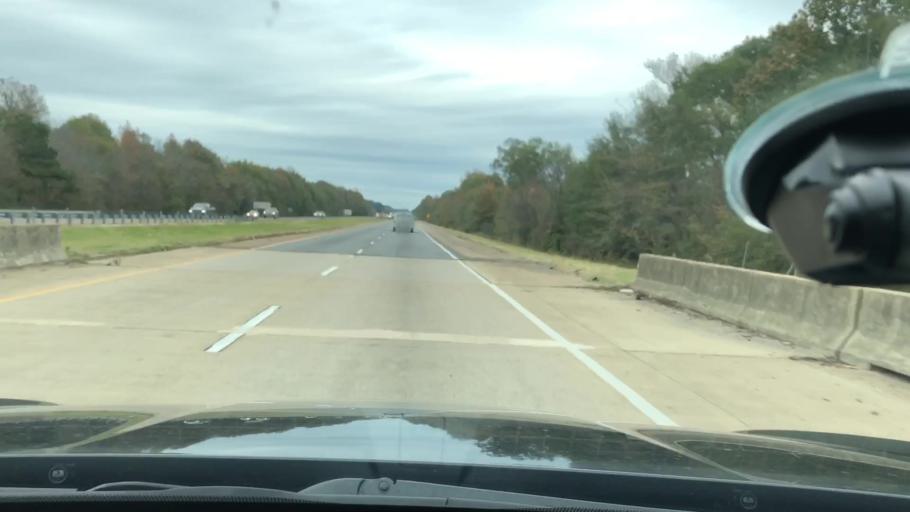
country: US
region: Arkansas
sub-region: Nevada County
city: Prescott
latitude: 33.8937
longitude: -93.3098
